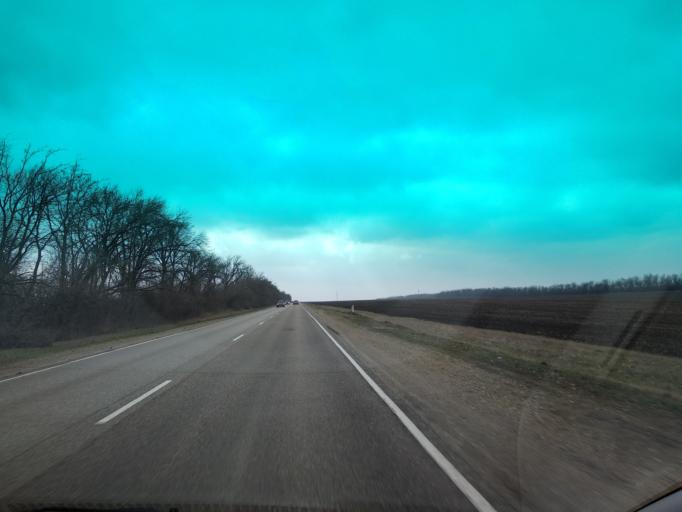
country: RU
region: Krasnodarskiy
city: Novomalorossiyskaya
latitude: 45.7483
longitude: 39.9191
